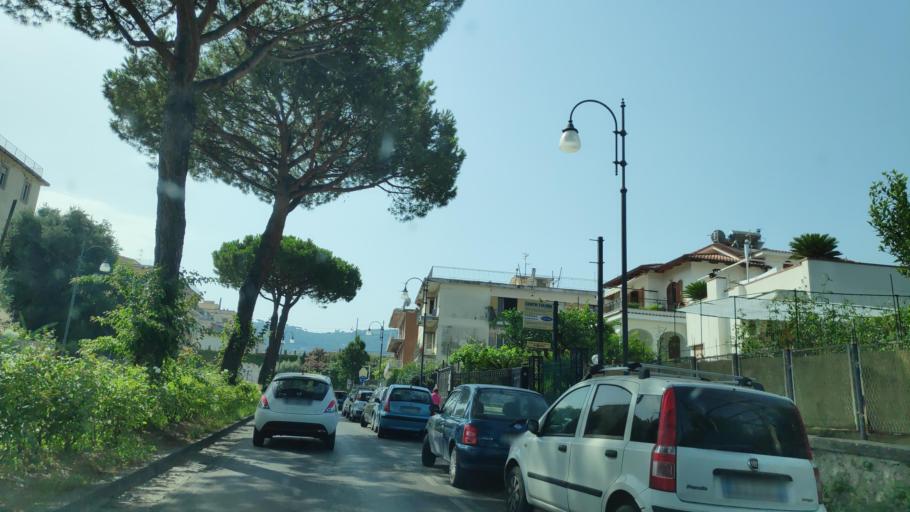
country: IT
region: Campania
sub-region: Provincia di Napoli
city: Sant'Agnello
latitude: 40.6324
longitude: 14.3977
